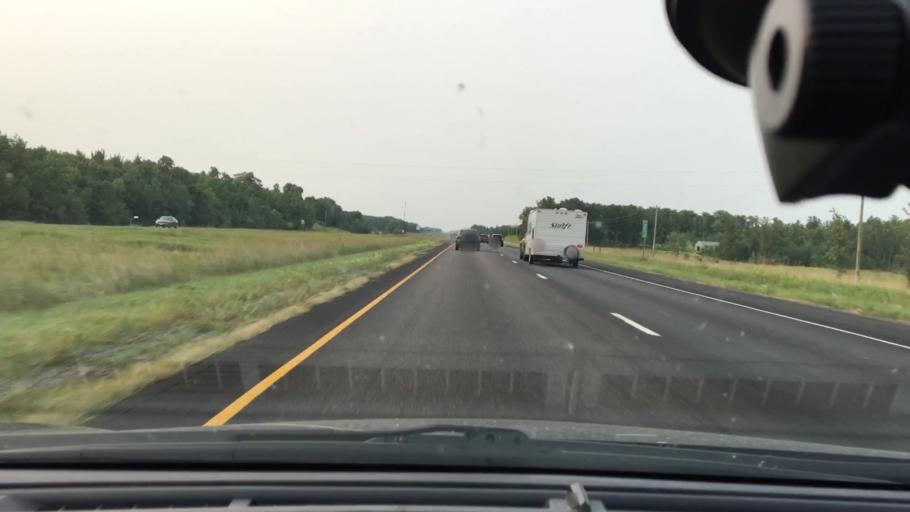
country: US
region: Minnesota
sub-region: Mille Lacs County
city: Milaca
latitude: 45.9198
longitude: -93.6630
